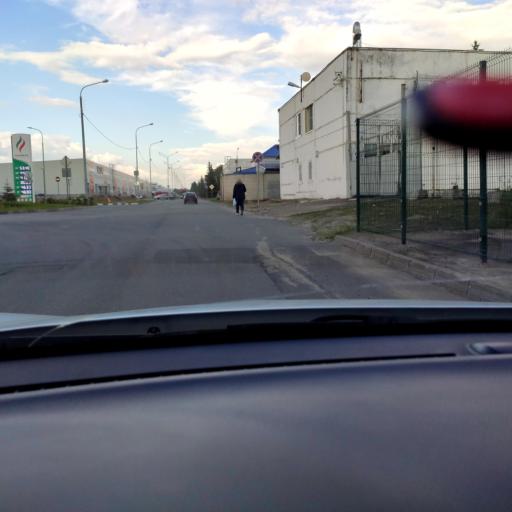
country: RU
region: Tatarstan
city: Staroye Arakchino
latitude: 55.8321
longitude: 49.0398
